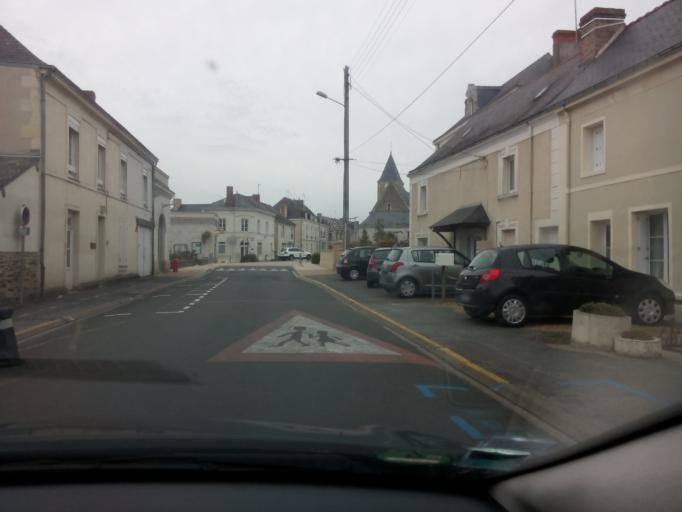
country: FR
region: Pays de la Loire
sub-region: Departement de Maine-et-Loire
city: Corne
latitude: 47.4709
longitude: -0.3491
